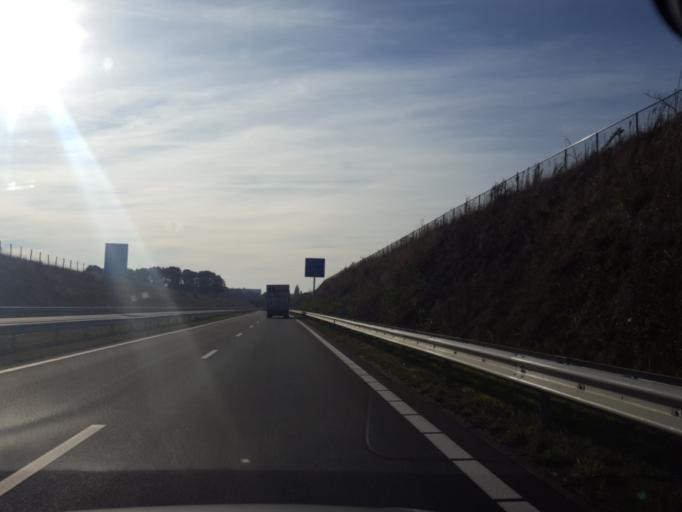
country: NL
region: Limburg
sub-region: Gemeente Onderbanken
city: Merkelbeek
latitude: 50.9420
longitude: 5.9417
